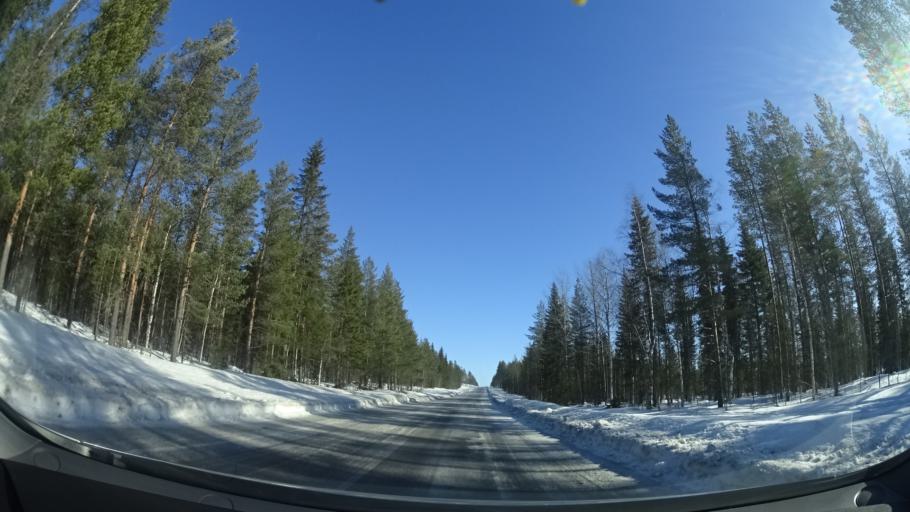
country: SE
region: Vaesterbotten
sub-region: Skelleftea Kommun
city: Langsele
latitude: 65.1241
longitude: 20.1122
